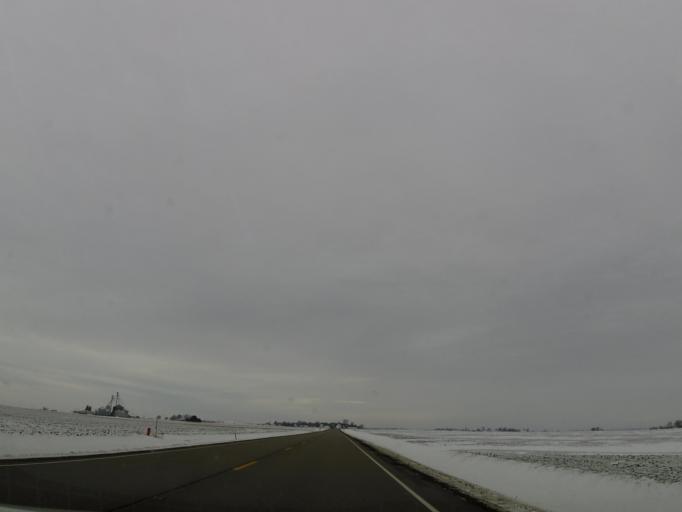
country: US
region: Illinois
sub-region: LaSalle County
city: Peru
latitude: 41.2577
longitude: -89.1524
